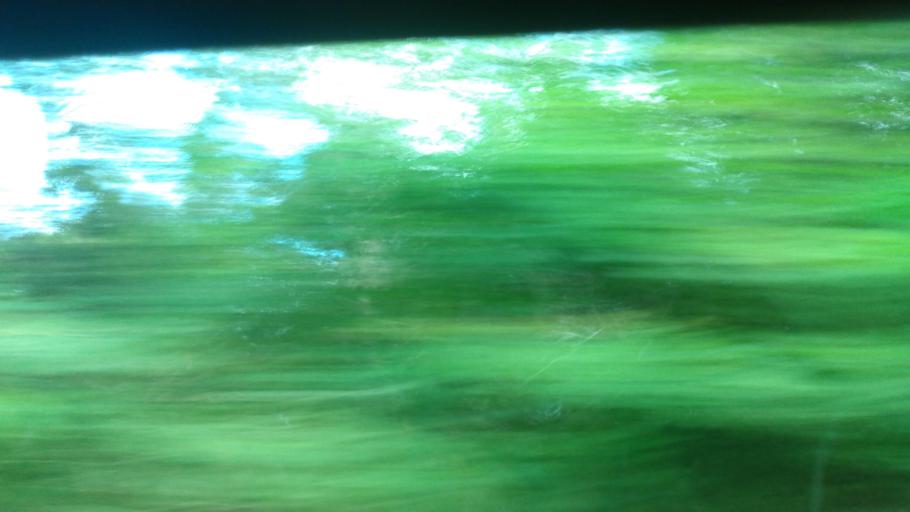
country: BR
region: Pernambuco
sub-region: Quipapa
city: Quipapa
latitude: -8.7843
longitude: -35.9518
